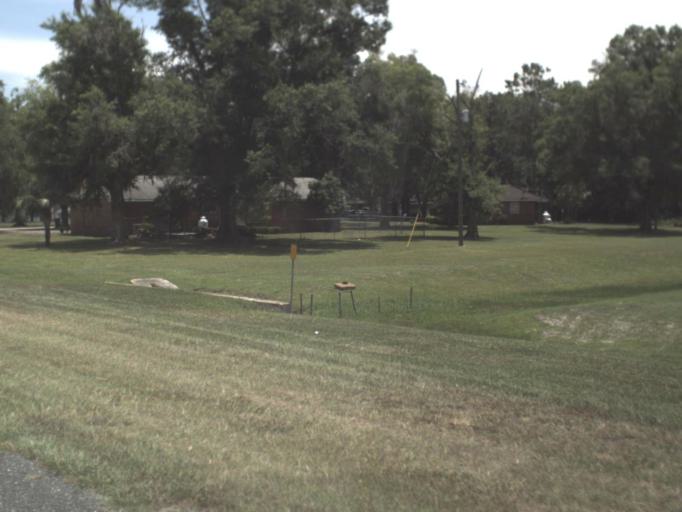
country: US
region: Florida
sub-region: Union County
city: Lake Butler
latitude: 30.0701
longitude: -82.2016
